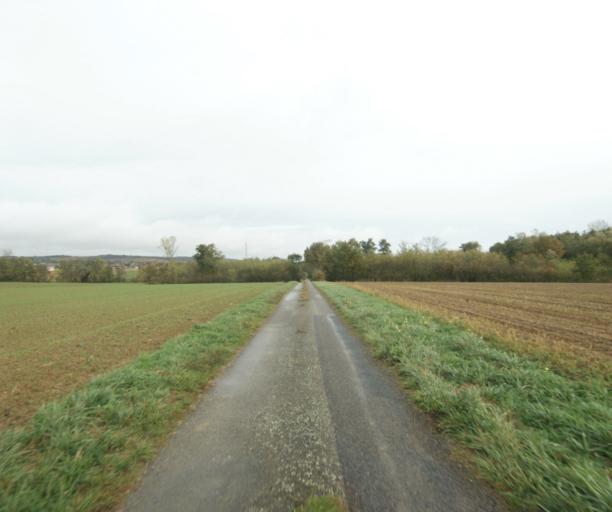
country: FR
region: Rhone-Alpes
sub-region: Departement de l'Ain
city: Pont-de-Vaux
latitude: 46.4865
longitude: 4.8899
